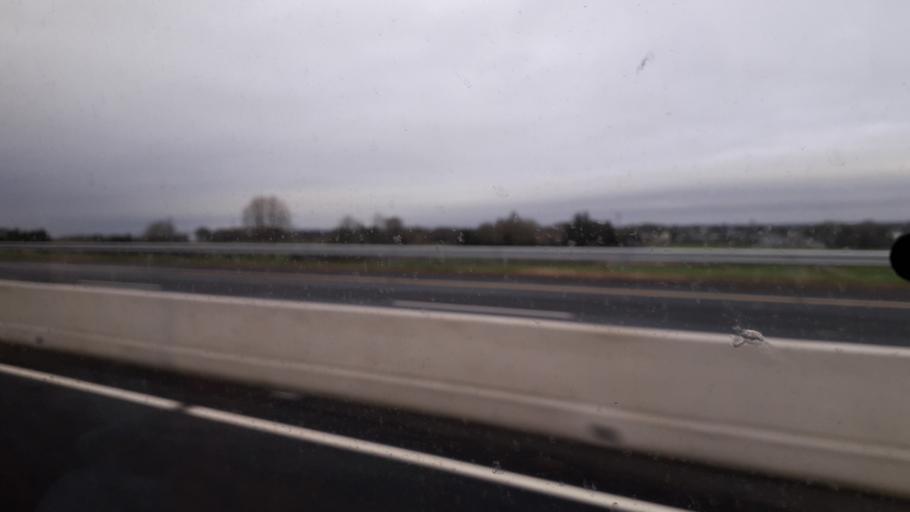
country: IE
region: Connaught
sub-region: County Galway
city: Athenry
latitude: 53.2804
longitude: -8.8018
